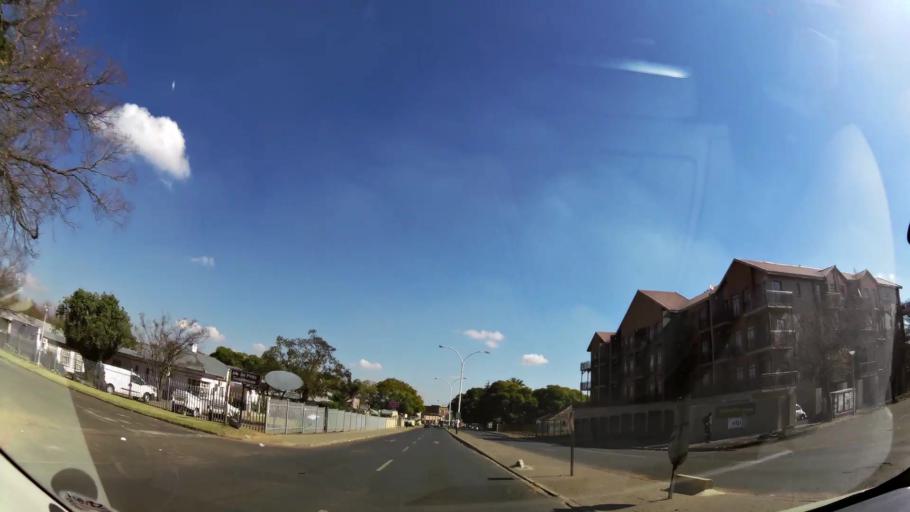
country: ZA
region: Mpumalanga
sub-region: Nkangala District Municipality
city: Witbank
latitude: -25.8758
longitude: 29.2231
